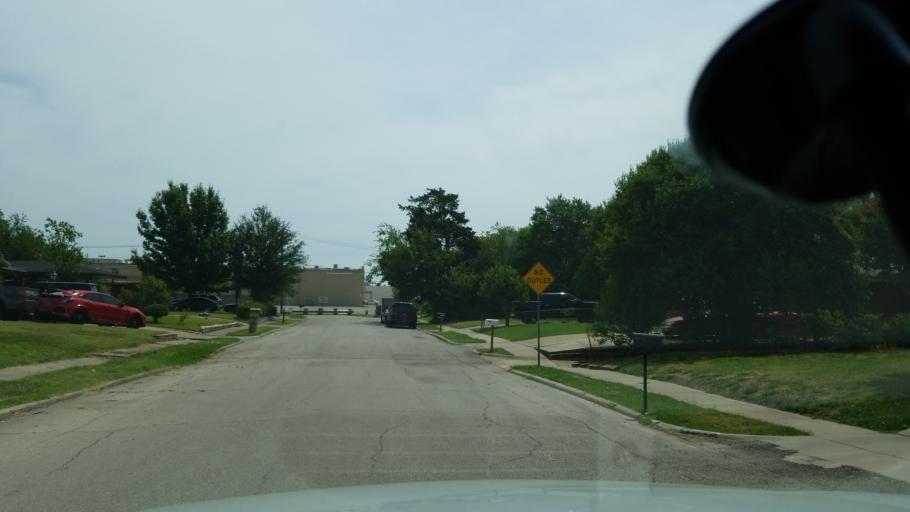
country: US
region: Texas
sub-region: Dallas County
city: Irving
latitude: 32.8295
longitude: -96.9864
